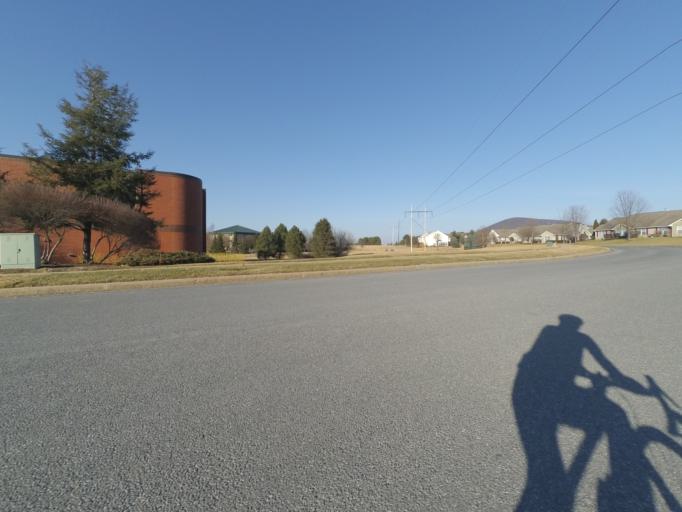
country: US
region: Pennsylvania
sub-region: Centre County
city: Lemont
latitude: 40.7862
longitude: -77.8234
